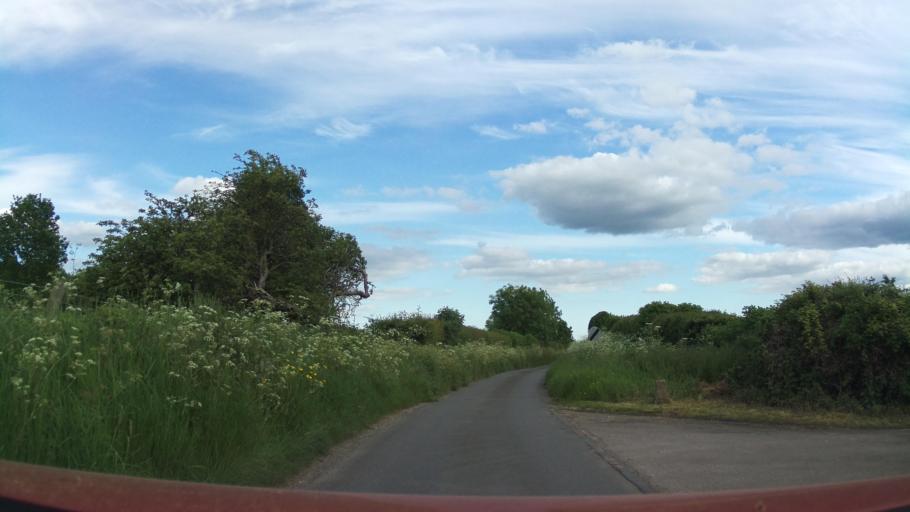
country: GB
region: England
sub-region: Gloucestershire
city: Chipping Campden
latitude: 52.0383
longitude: -1.7288
